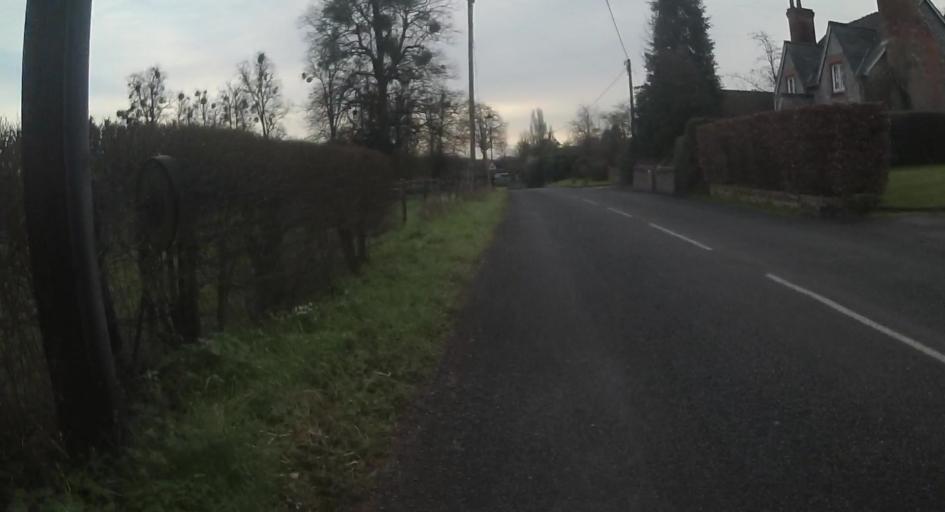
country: GB
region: England
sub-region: Hampshire
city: Overton
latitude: 51.2186
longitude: -1.3746
